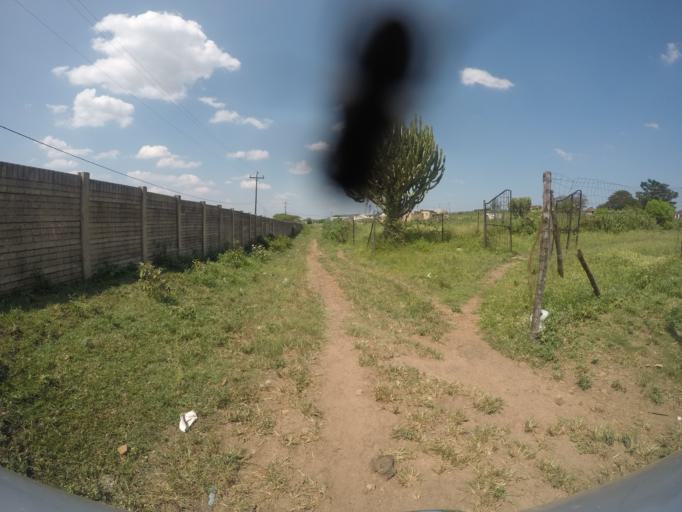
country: ZA
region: KwaZulu-Natal
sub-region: uThungulu District Municipality
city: Empangeni
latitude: -28.5879
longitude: 31.7415
